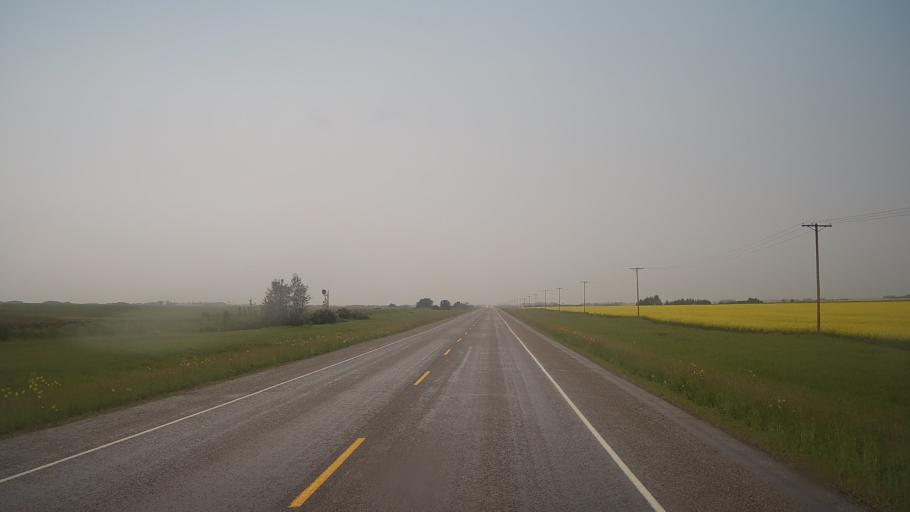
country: CA
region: Saskatchewan
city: Biggar
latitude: 52.1487
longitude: -108.2226
